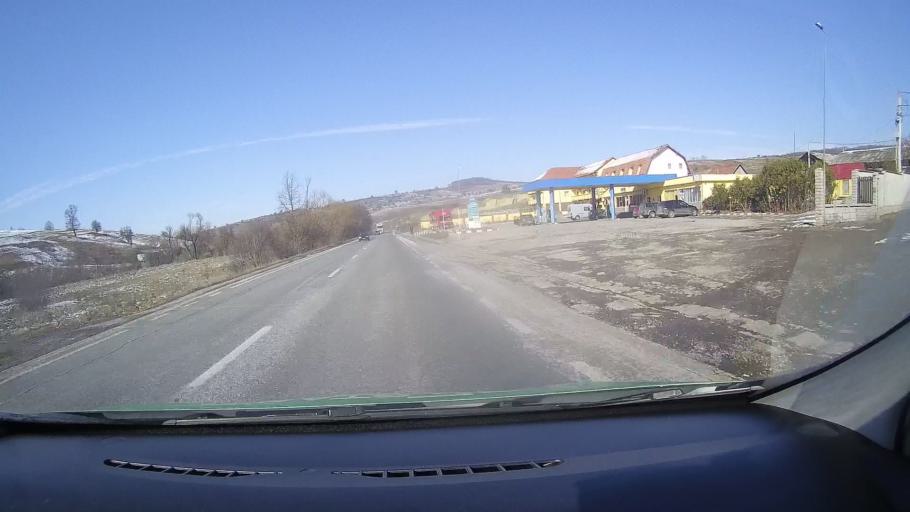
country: RO
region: Brasov
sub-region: Oras Rupea
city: Rupea
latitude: 46.0386
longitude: 25.2029
